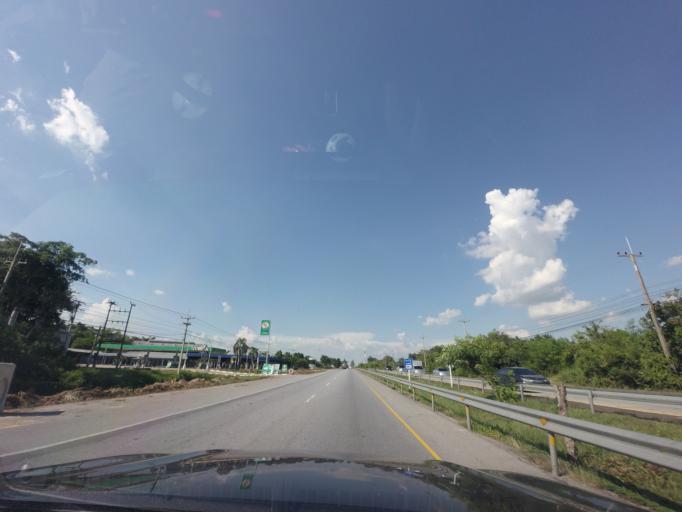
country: TH
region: Nakhon Ratchasima
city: Sida
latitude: 15.5305
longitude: 102.5439
